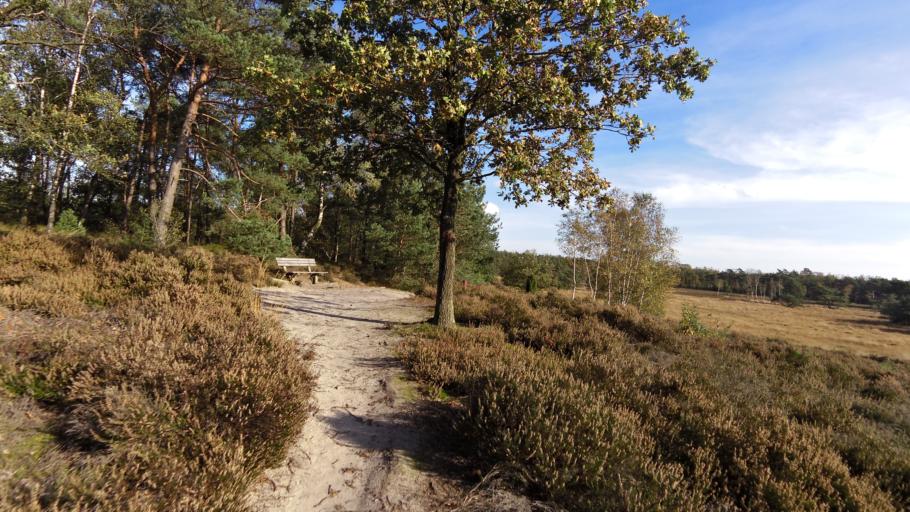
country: NL
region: Gelderland
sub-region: Gemeente Epe
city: Emst
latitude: 52.3428
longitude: 5.9050
